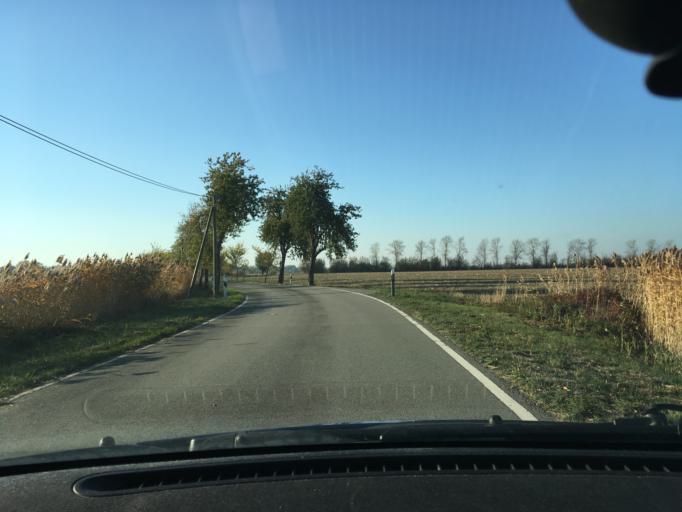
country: DE
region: Lower Saxony
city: Hitzacker
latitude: 53.1850
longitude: 11.0316
